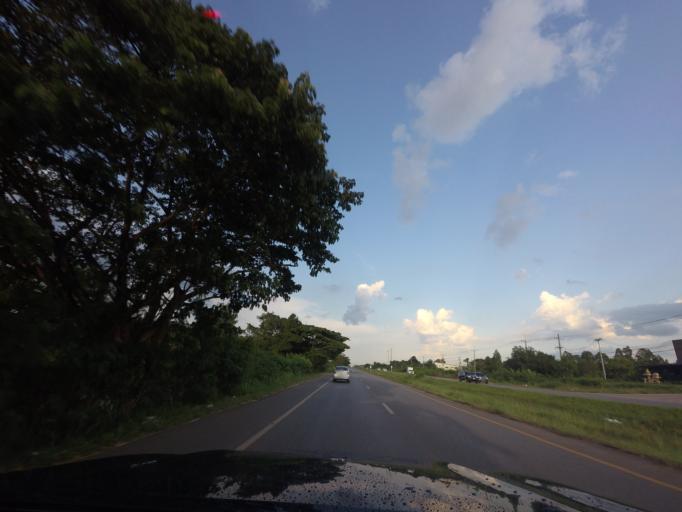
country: TH
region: Khon Kaen
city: Khon Kaen
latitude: 16.3935
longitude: 102.8503
